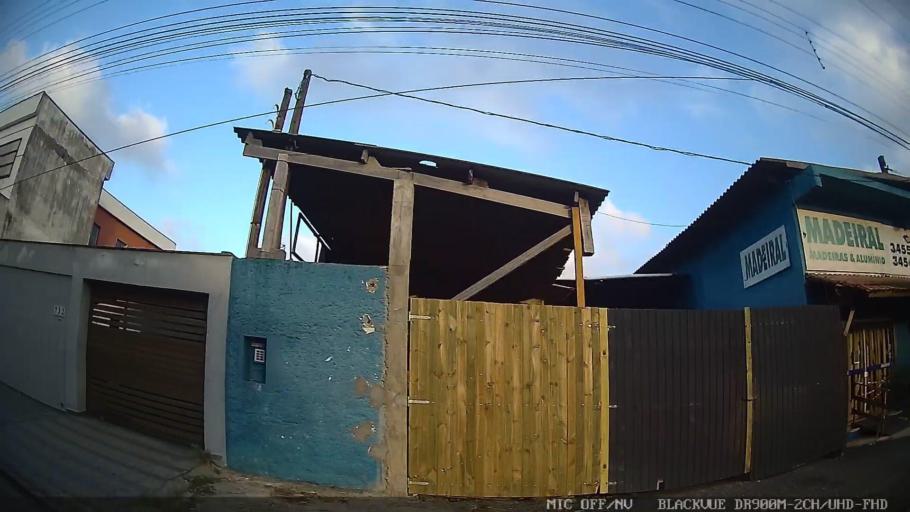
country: BR
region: Sao Paulo
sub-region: Peruibe
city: Peruibe
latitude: -24.3144
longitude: -47.0019
